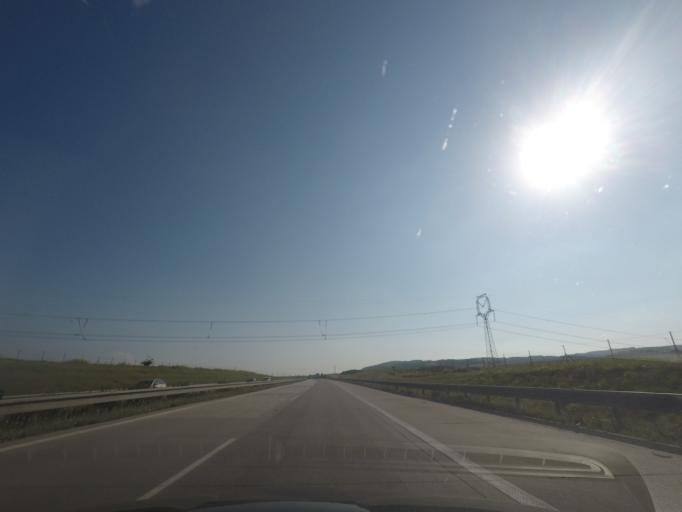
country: CZ
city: Fulnek
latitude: 49.6821
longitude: 17.9389
